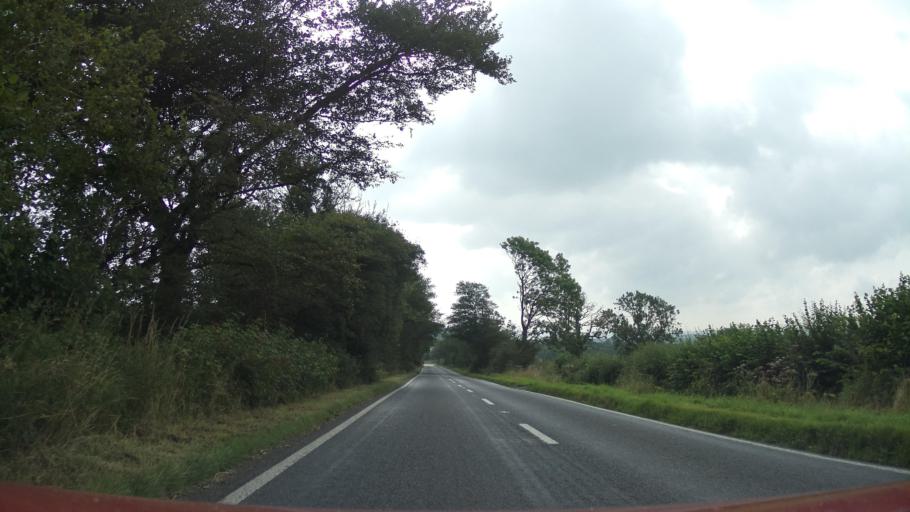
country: GB
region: England
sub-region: Somerset
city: Shepton Mallet
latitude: 51.2068
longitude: -2.4962
